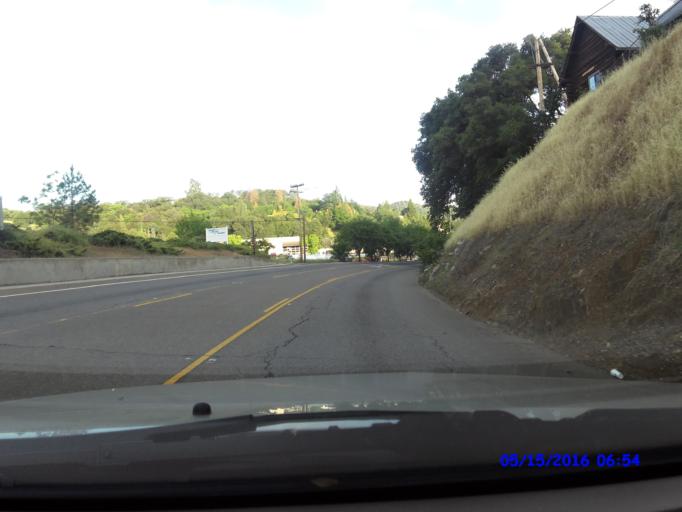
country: US
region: California
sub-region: Tuolumne County
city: Sonora
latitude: 37.9754
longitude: -120.3772
